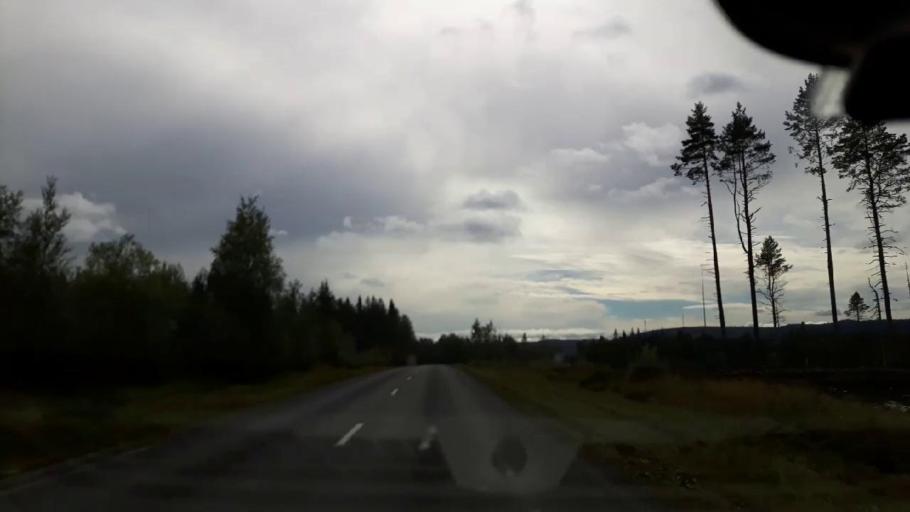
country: SE
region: Jaemtland
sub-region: Ragunda Kommun
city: Hammarstrand
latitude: 63.1062
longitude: 15.9109
